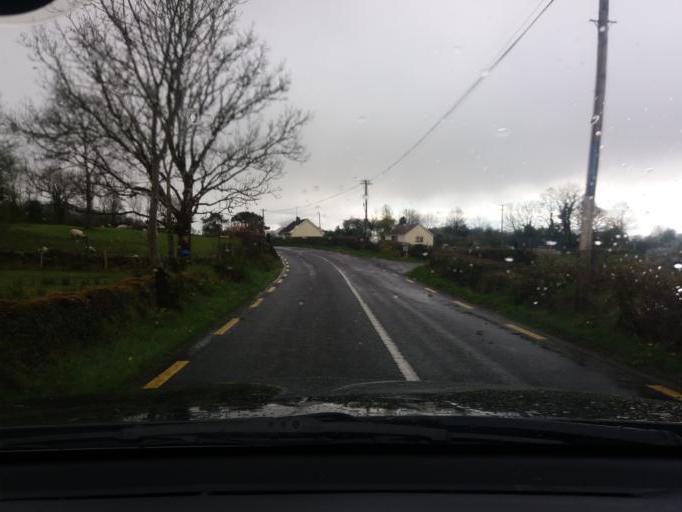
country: IE
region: Connaught
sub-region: County Leitrim
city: Manorhamilton
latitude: 54.2664
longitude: -7.9422
